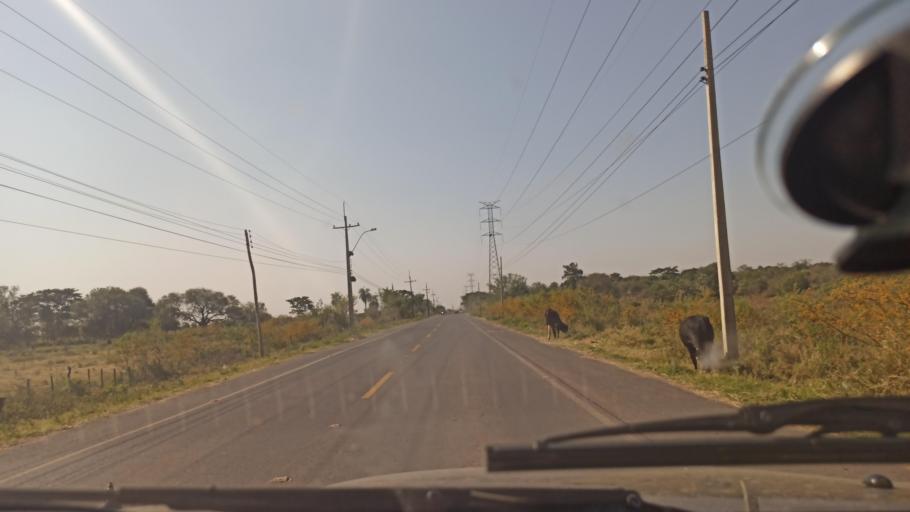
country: PY
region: Presidente Hayes
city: Nanawa
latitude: -25.2660
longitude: -57.6878
